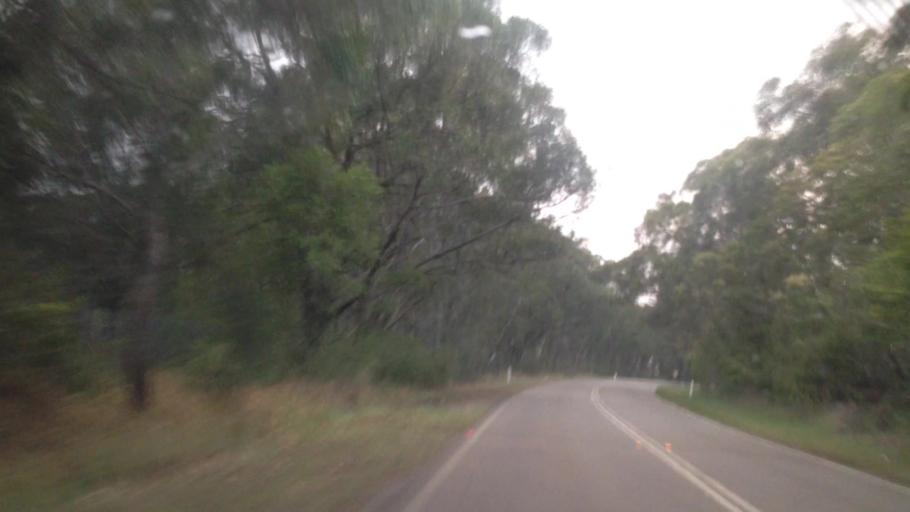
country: AU
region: New South Wales
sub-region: Lake Macquarie Shire
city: Dora Creek
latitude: -33.1095
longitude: 151.4774
